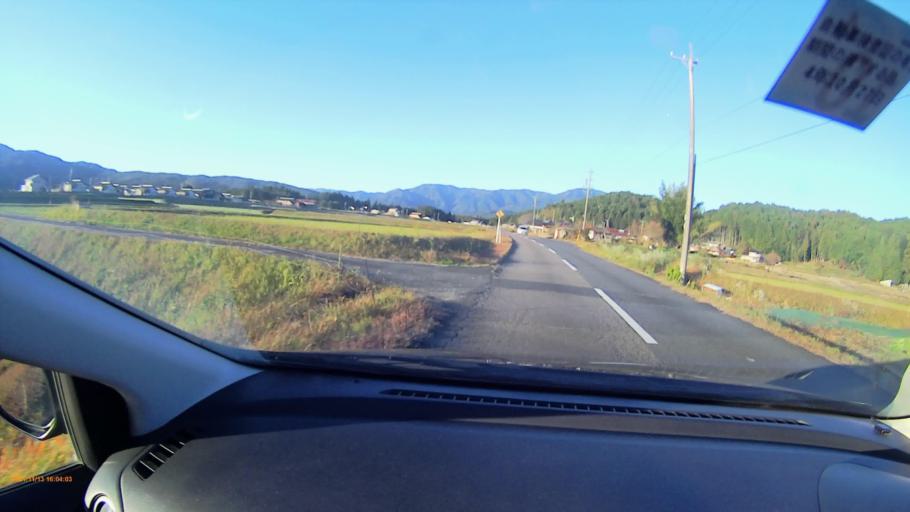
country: JP
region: Gifu
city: Nakatsugawa
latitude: 35.5899
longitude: 137.4698
